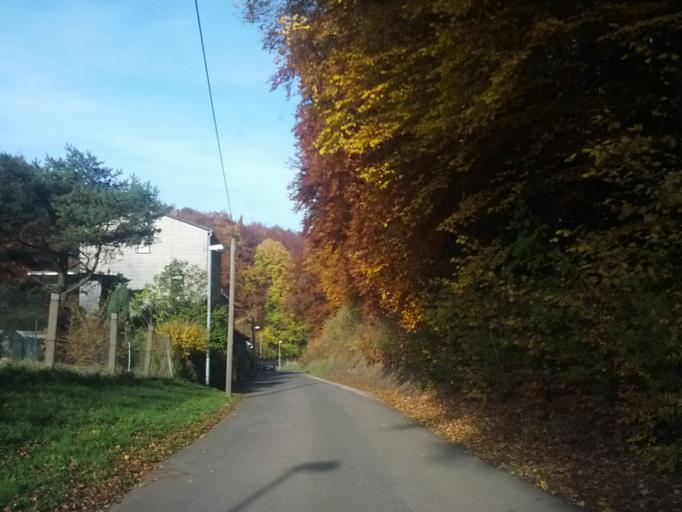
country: DE
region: Thuringia
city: Thal
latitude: 50.9204
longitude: 10.3715
